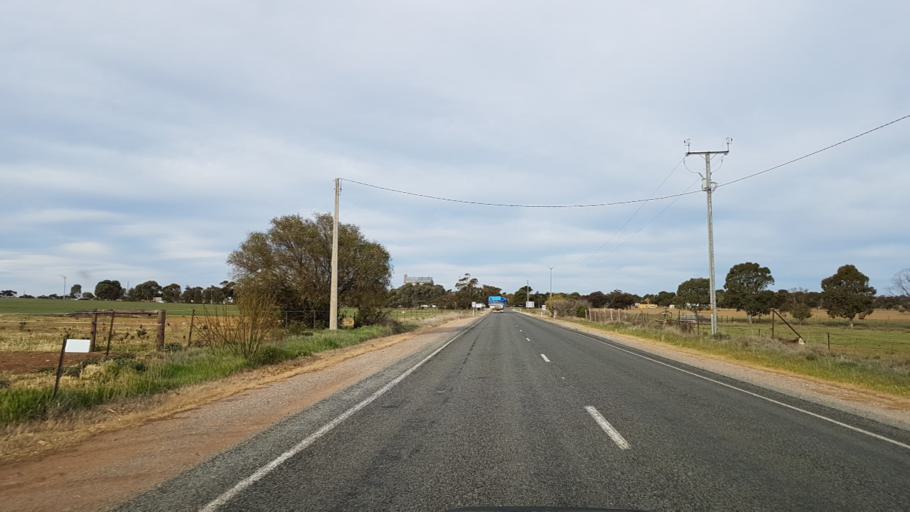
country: AU
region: South Australia
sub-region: Peterborough
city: Peterborough
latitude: -33.0299
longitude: 138.7417
